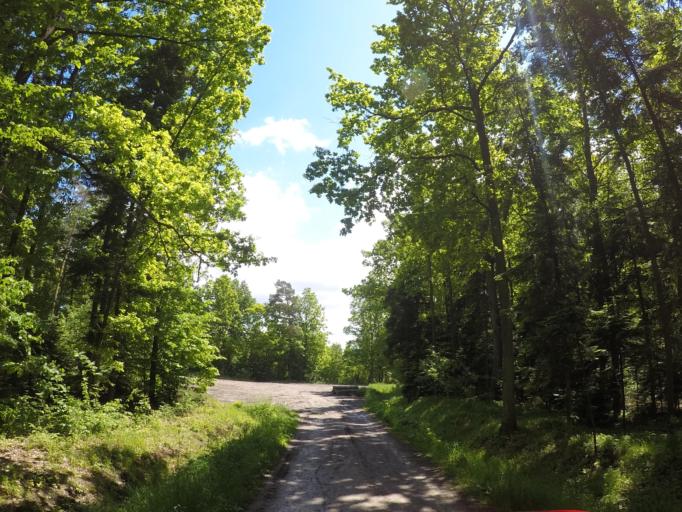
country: PL
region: Swietokrzyskie
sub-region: Powiat kielecki
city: Domaszowice
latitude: 50.9101
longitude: 20.6611
